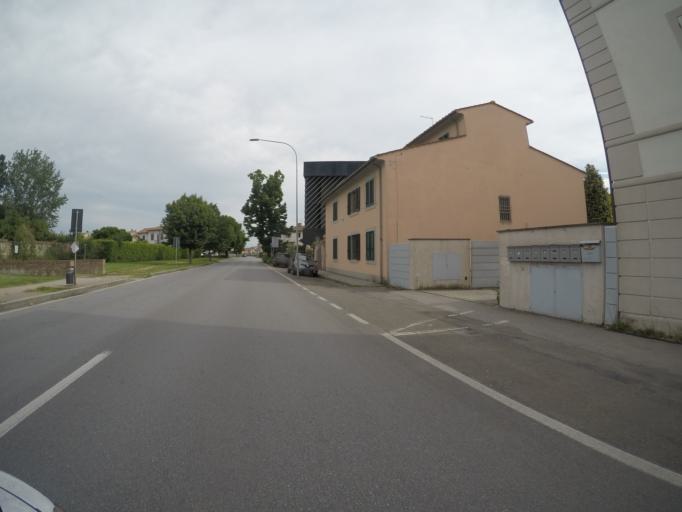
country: IT
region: Tuscany
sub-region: Province of Pisa
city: Madonna dell'Acqua
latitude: 43.7284
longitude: 10.3889
